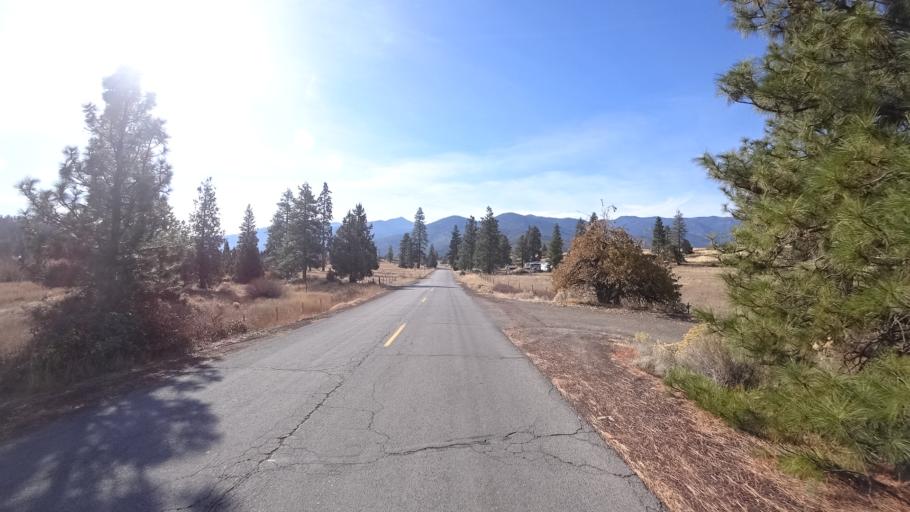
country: US
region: California
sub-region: Siskiyou County
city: Weed
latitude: 41.4472
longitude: -122.4327
